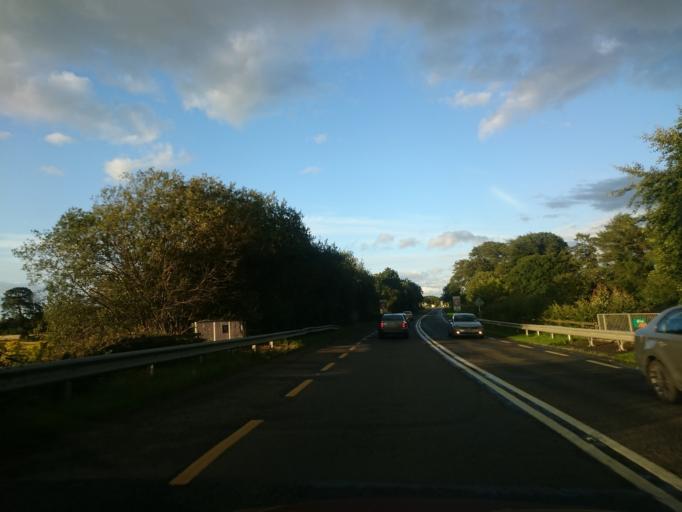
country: IE
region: Leinster
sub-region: Loch Garman
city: Ferns
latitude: 52.6102
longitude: -6.4407
